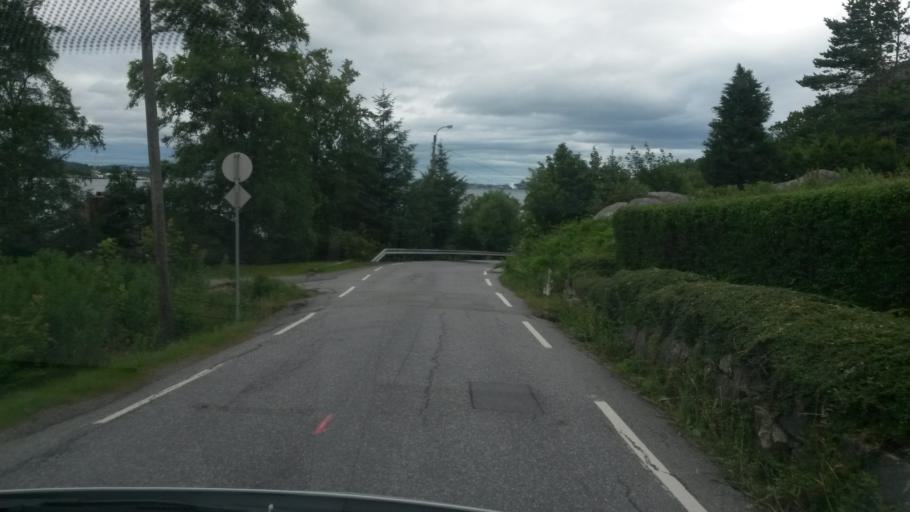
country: NO
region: Rogaland
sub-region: Sandnes
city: Sandnes
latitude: 58.8813
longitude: 5.7755
